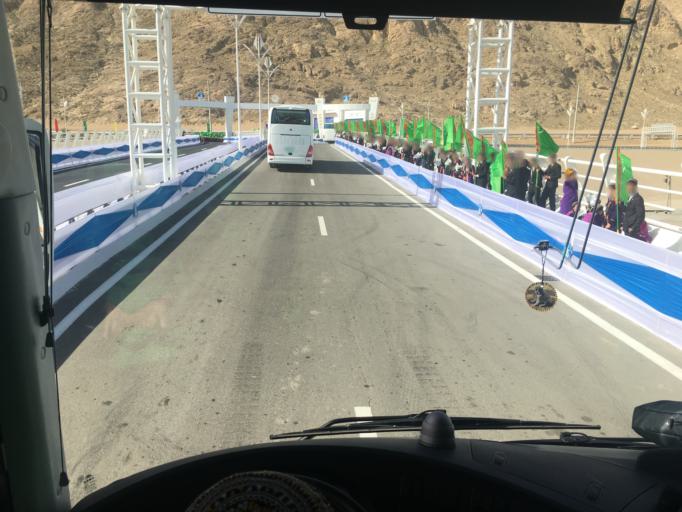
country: TM
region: Balkan
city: Turkmenbasy
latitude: 40.0065
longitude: 53.0241
